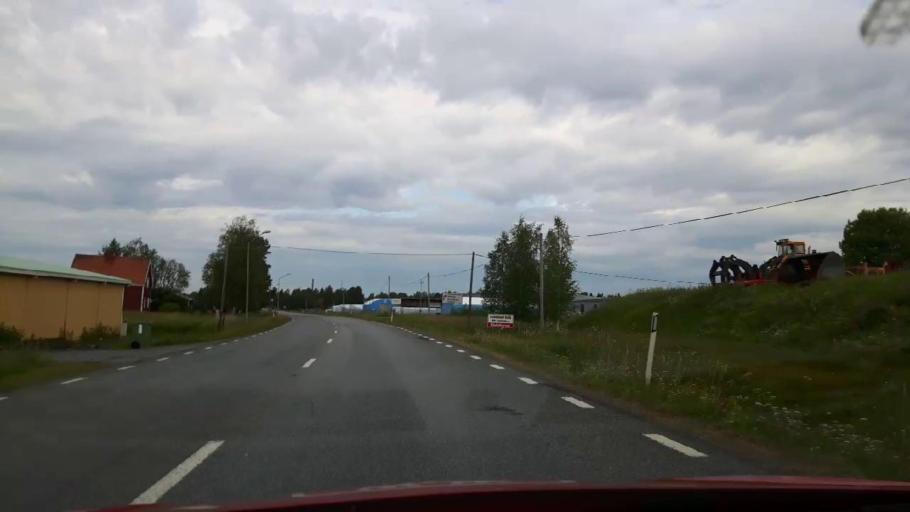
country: SE
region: Jaemtland
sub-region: Stroemsunds Kommun
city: Stroemsund
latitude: 63.5698
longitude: 15.3621
